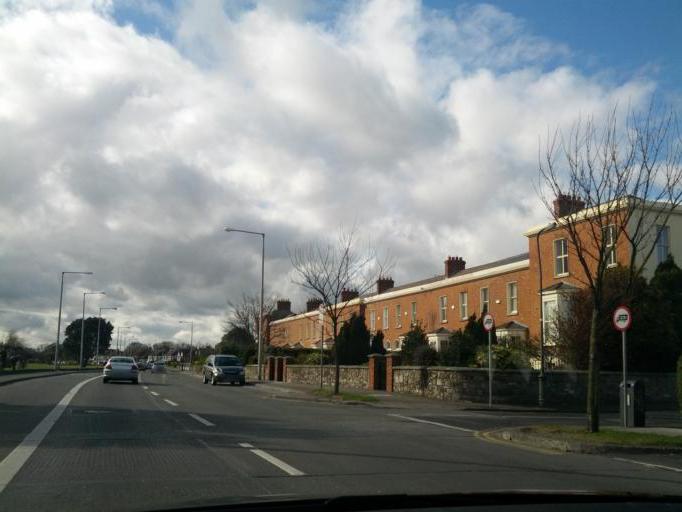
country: IE
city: Killester
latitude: 53.3596
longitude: -6.1991
